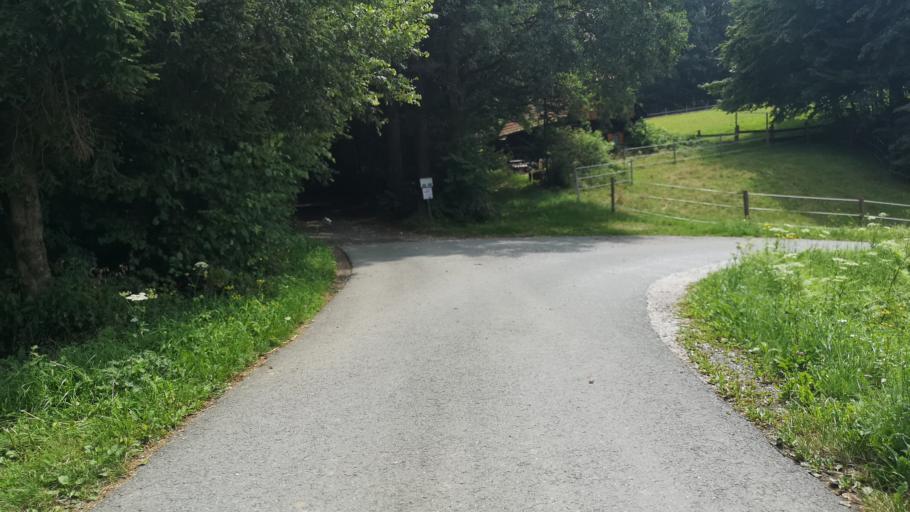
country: AT
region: Styria
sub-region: Politischer Bezirk Leibnitz
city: Weitendorf
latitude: 46.8720
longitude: 15.4662
